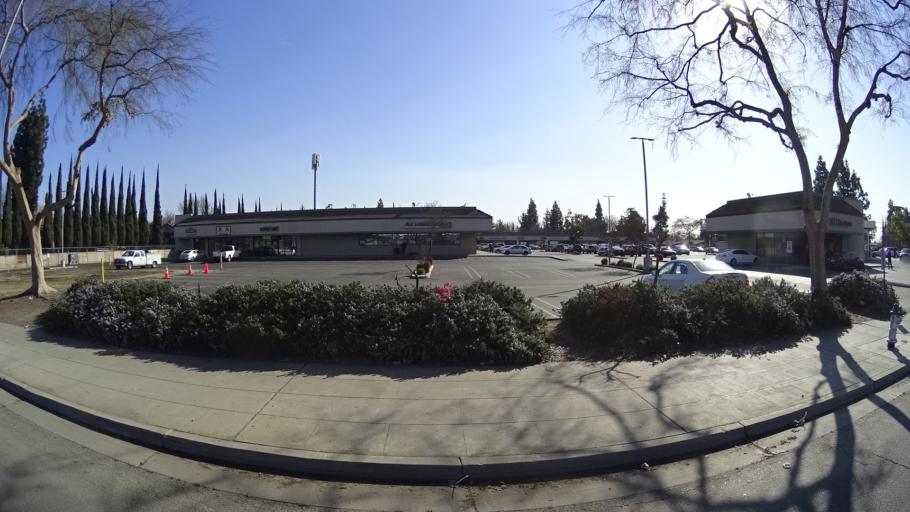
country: US
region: California
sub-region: Fresno County
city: Fresno
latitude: 36.7296
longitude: -119.7364
